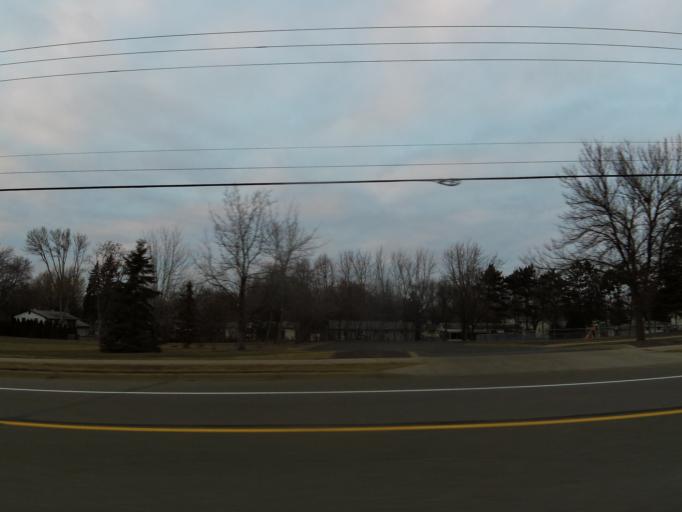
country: US
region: Minnesota
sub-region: Washington County
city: Birchwood
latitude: 45.0502
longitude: -92.9990
